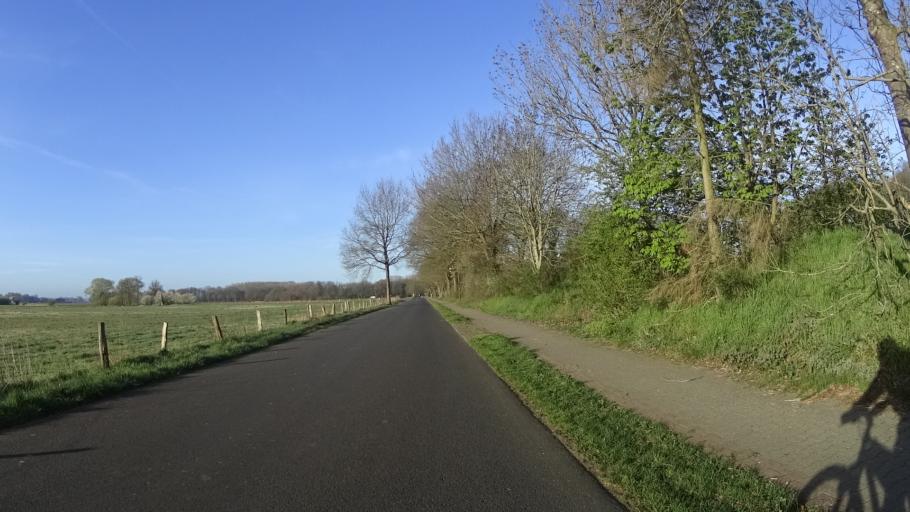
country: DE
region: Lower Saxony
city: Lathen
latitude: 52.8598
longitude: 7.3103
